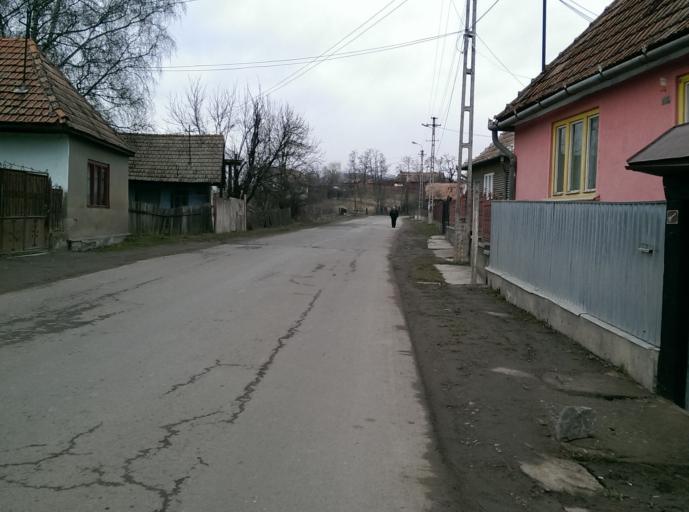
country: RO
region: Cluj
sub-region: Comuna Iara
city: Iara
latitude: 46.5570
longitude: 23.5118
